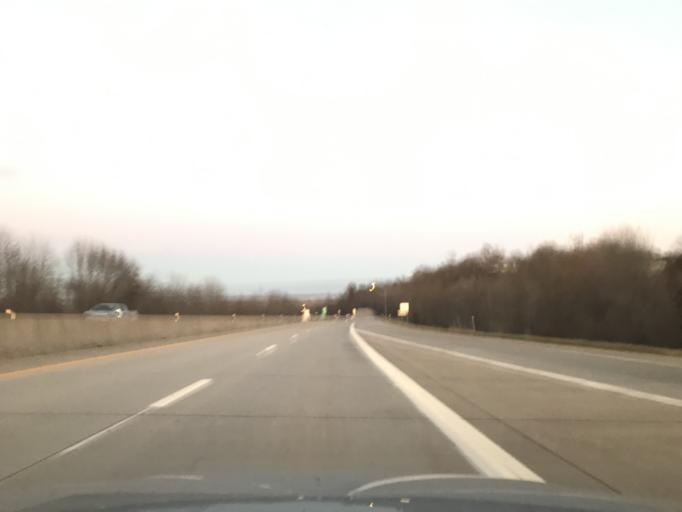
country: US
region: Missouri
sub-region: Marion County
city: Hannibal
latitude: 39.7179
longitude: -91.3685
